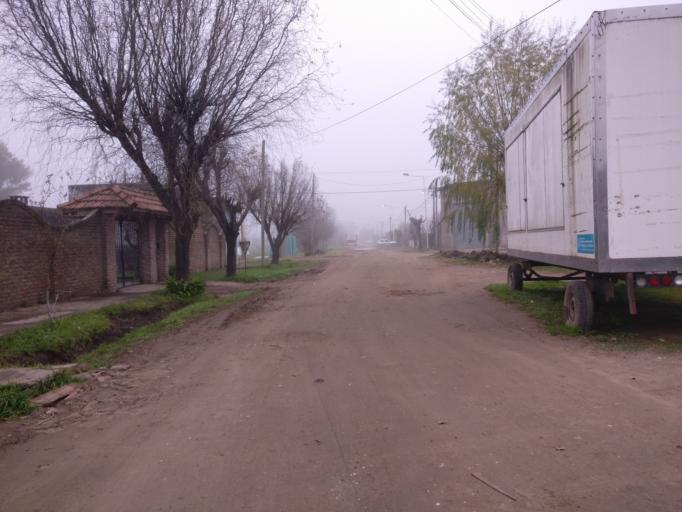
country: AR
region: Buenos Aires
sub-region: Partido de Ezeiza
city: Ezeiza
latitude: -34.9427
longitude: -58.6161
